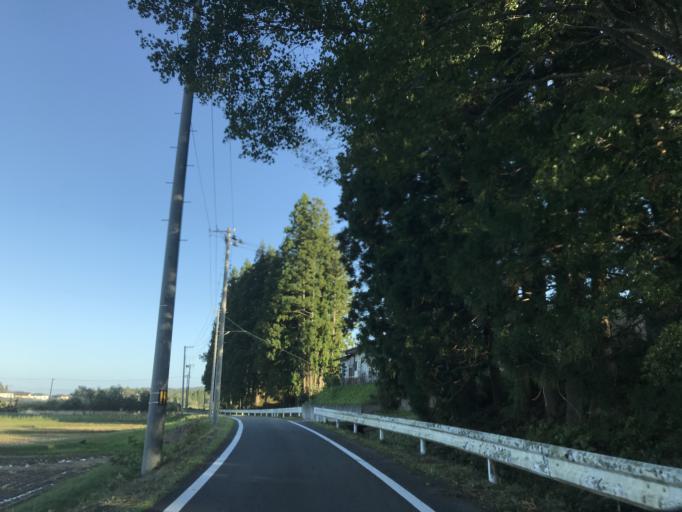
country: JP
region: Iwate
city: Ichinoseki
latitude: 38.9422
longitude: 141.0459
